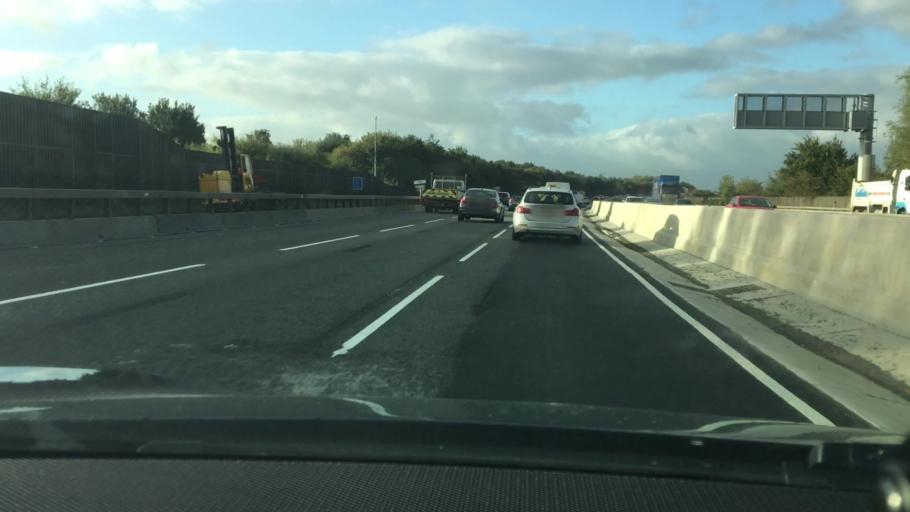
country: GB
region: England
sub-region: Derbyshire
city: Long Eaton
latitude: 52.8939
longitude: -1.3000
